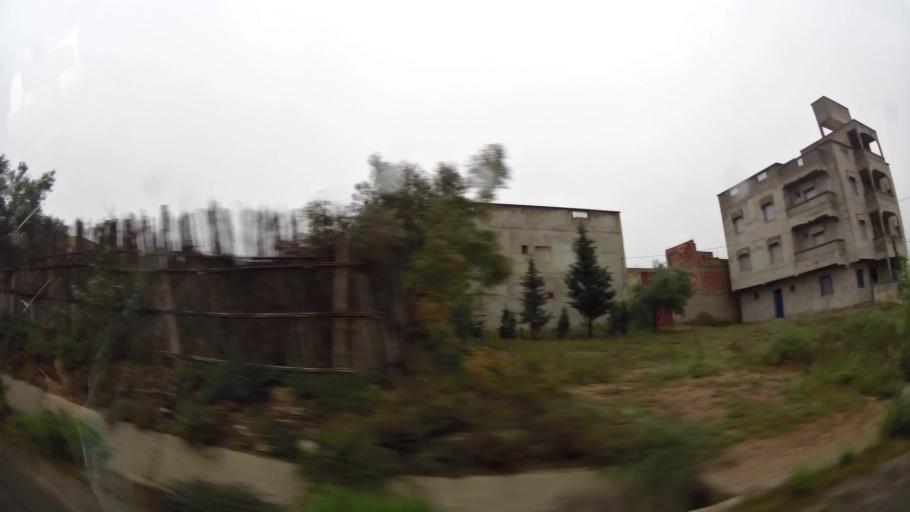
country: MA
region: Oriental
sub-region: Nador
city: Boudinar
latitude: 35.1233
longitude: -3.5757
